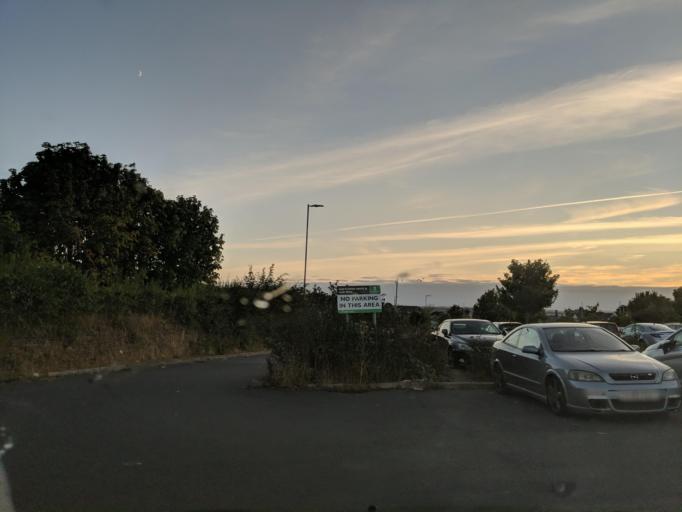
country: GB
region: England
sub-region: Plymouth
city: Plymouth
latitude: 50.3858
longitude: -4.1536
